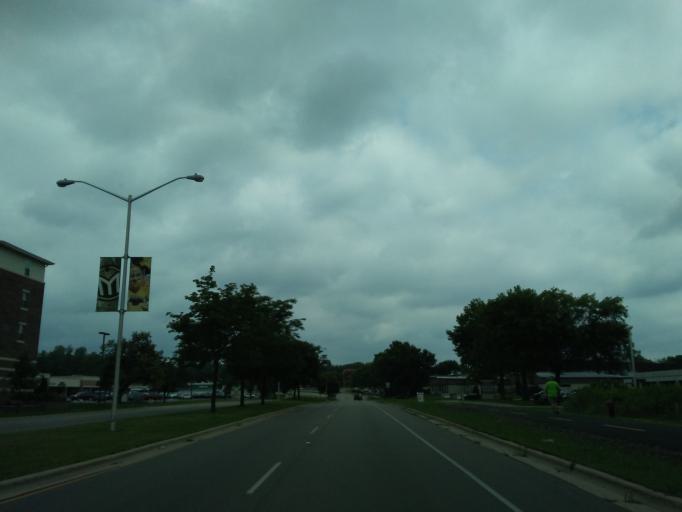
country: US
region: Wisconsin
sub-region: Dane County
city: Middleton
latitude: 43.1007
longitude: -89.4862
